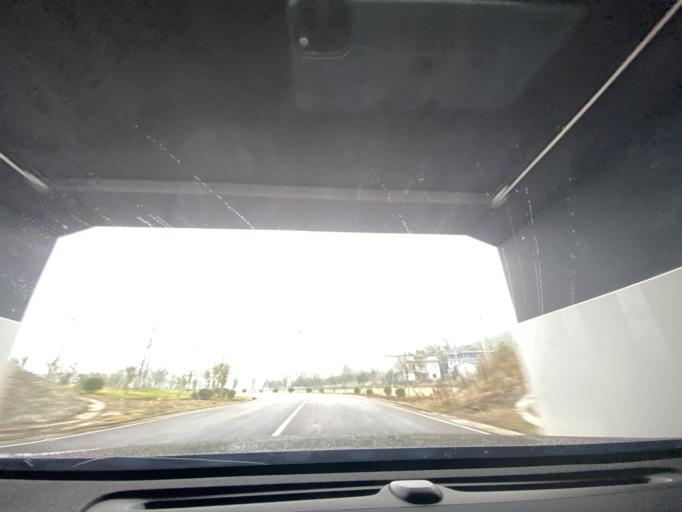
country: CN
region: Sichuan
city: Jiancheng
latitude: 30.3951
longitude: 104.6335
